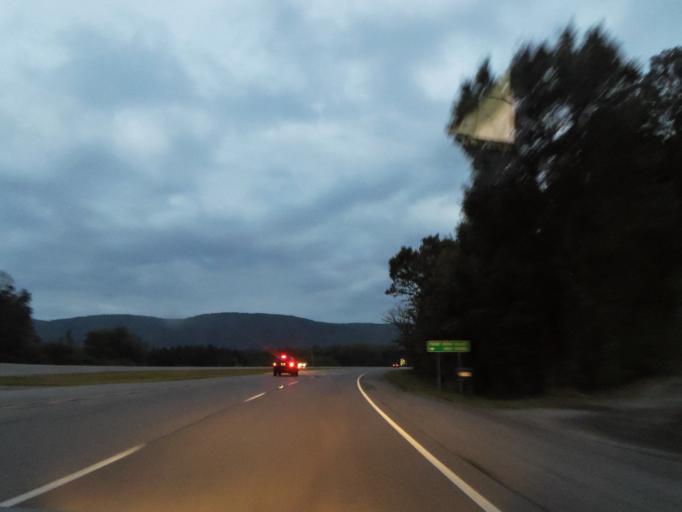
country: US
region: Alabama
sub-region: Madison County
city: Owens Cross Roads
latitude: 34.6815
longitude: -86.3325
